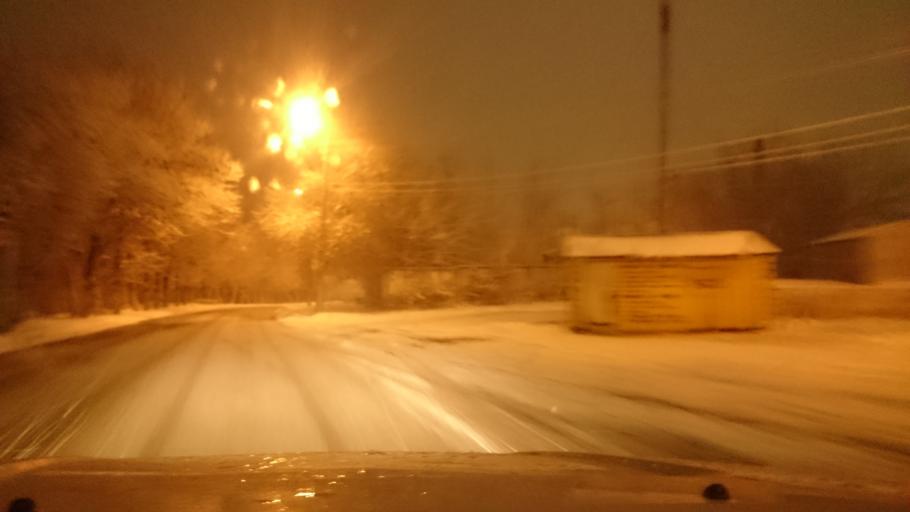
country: RU
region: Tula
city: Mendeleyevskiy
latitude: 54.1625
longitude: 37.5701
